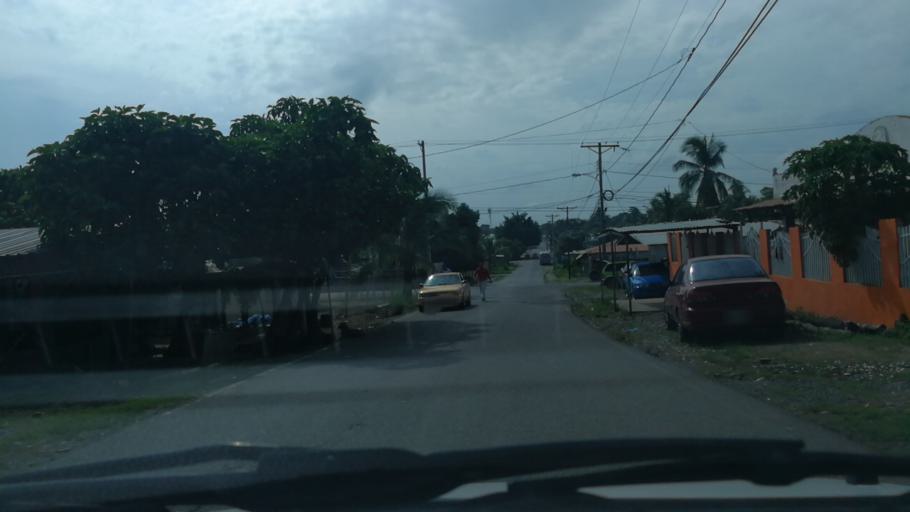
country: PA
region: Panama
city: Pacora
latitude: 9.0828
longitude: -79.2937
